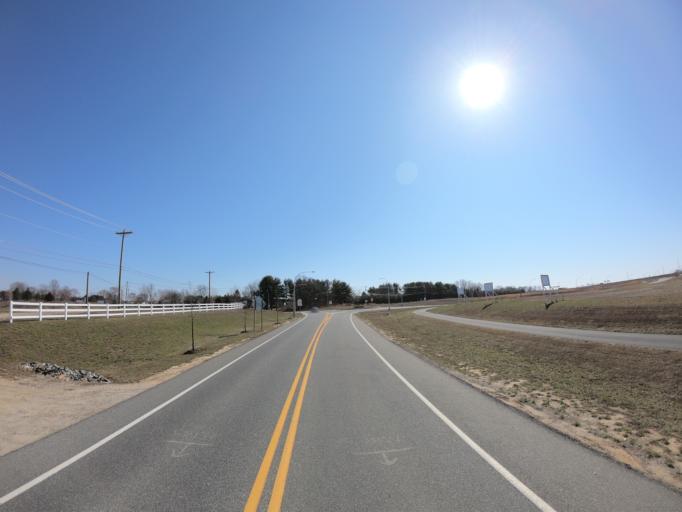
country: US
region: Delaware
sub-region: New Castle County
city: Middletown
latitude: 39.5306
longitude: -75.6792
